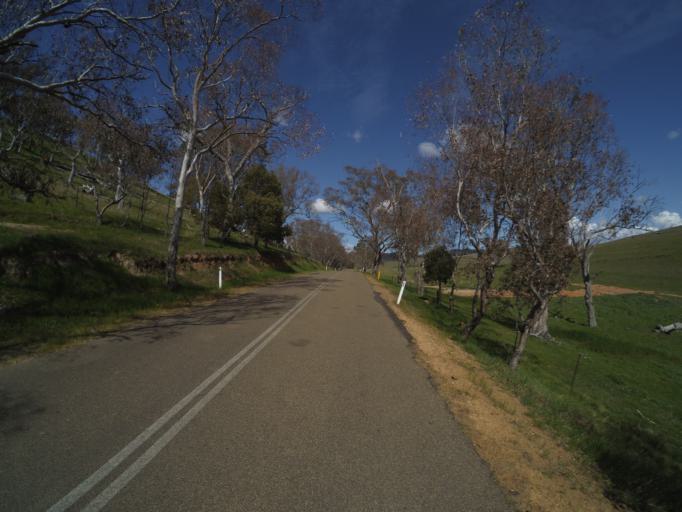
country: AU
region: New South Wales
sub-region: Yass Valley
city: Yass
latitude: -35.0080
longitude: 148.8501
